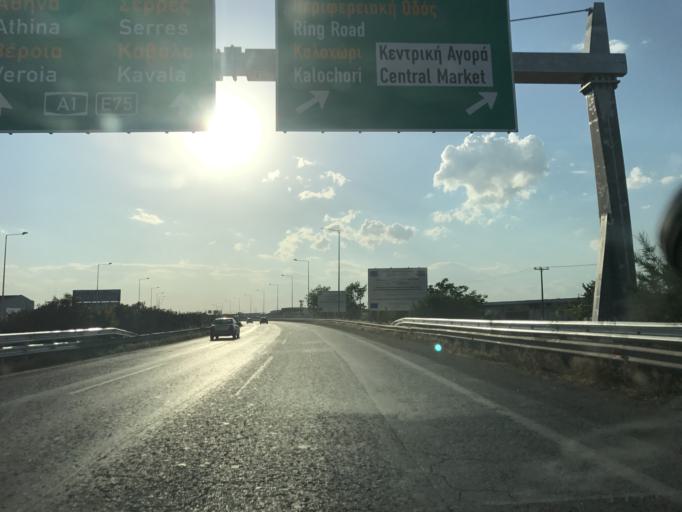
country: GR
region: Central Macedonia
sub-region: Nomos Thessalonikis
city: Menemeni
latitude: 40.6552
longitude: 22.8926
